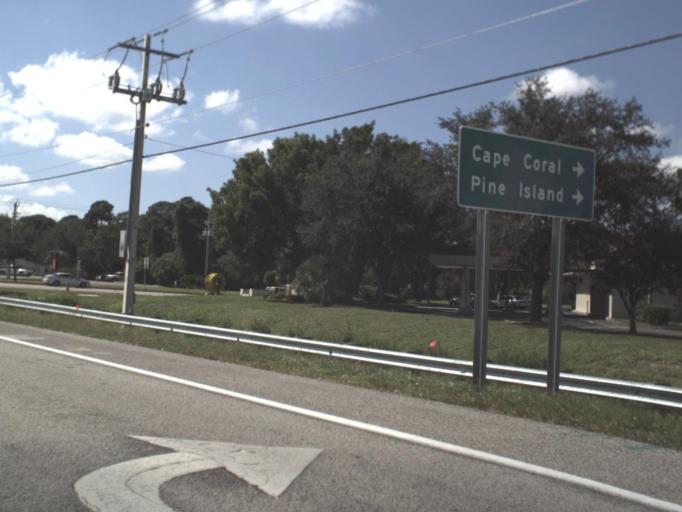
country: US
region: Florida
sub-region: Lee County
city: Palmona Park
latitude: 26.6832
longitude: -81.9018
